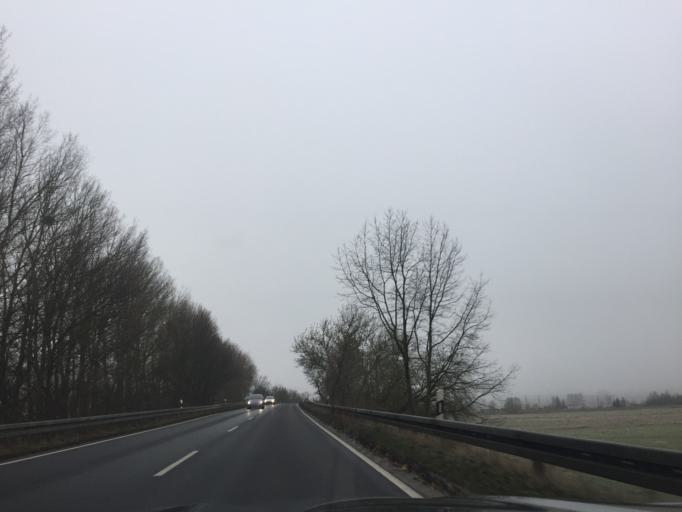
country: DE
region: Brandenburg
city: Velten
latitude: 52.6443
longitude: 13.1475
